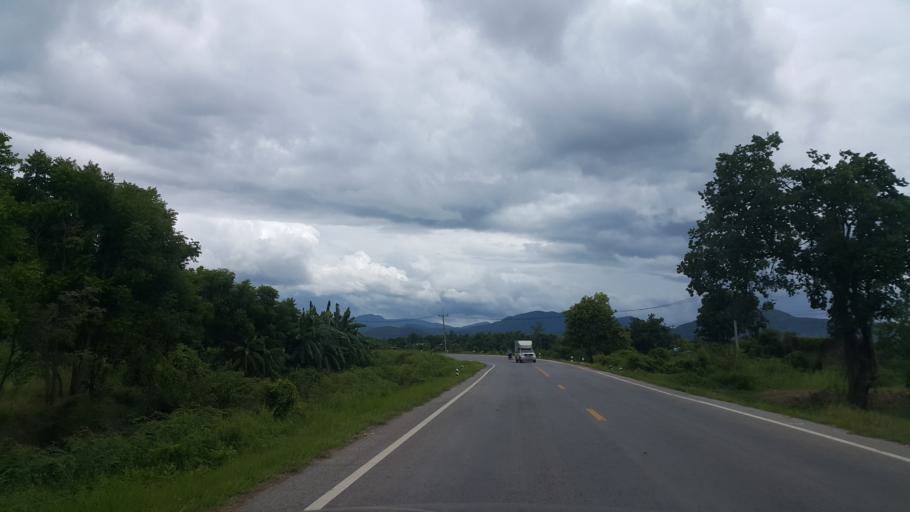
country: TH
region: Sukhothai
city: Ban Na
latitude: 17.0516
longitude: 99.7044
